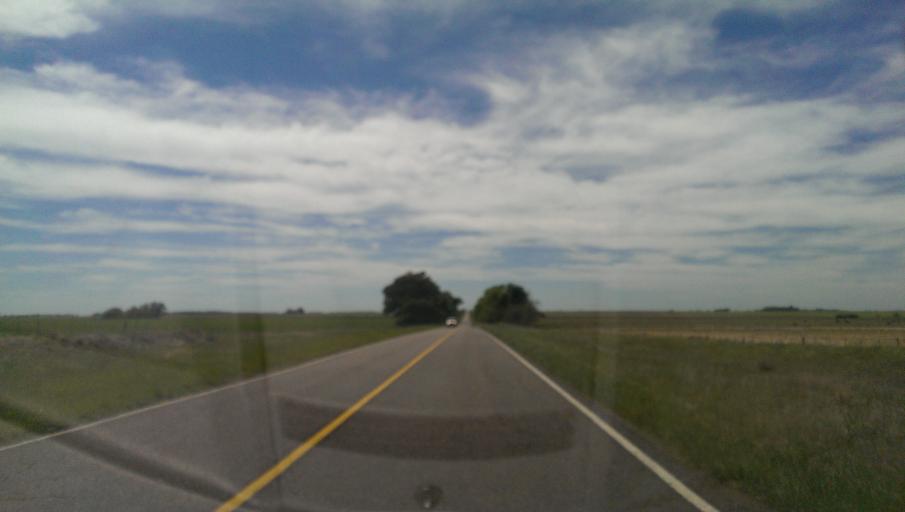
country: AR
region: Buenos Aires
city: Coronel Pringles
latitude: -37.7104
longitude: -61.5833
